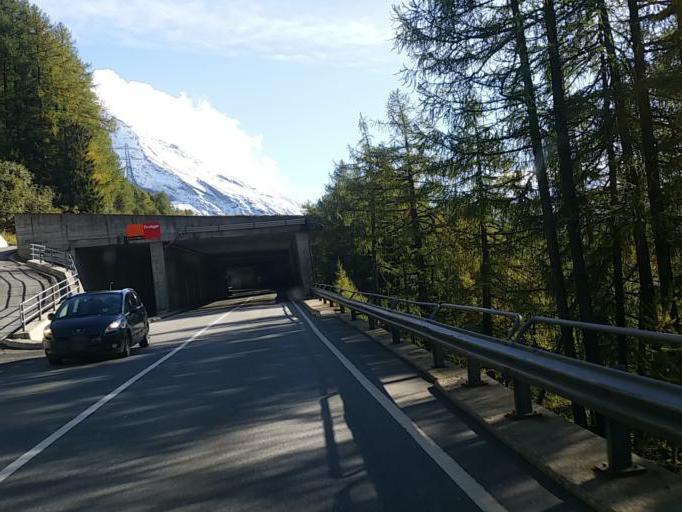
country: CH
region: Valais
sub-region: Brig District
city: Brig
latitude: 46.2685
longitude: 8.0403
